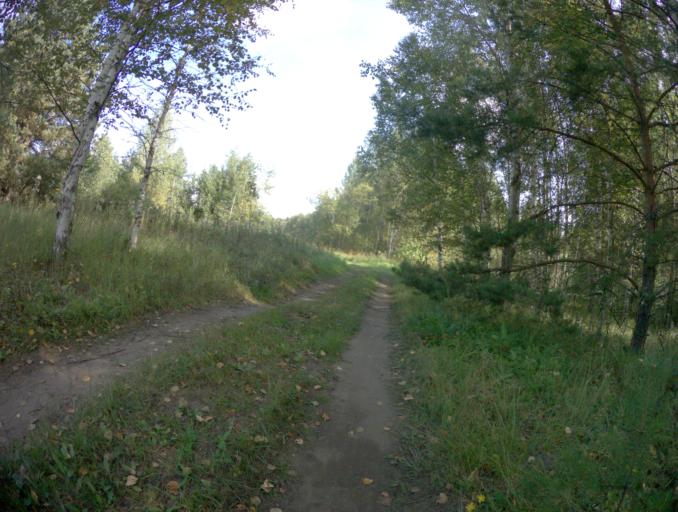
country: RU
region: Vladimir
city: Pokrov
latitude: 55.8442
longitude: 39.1946
